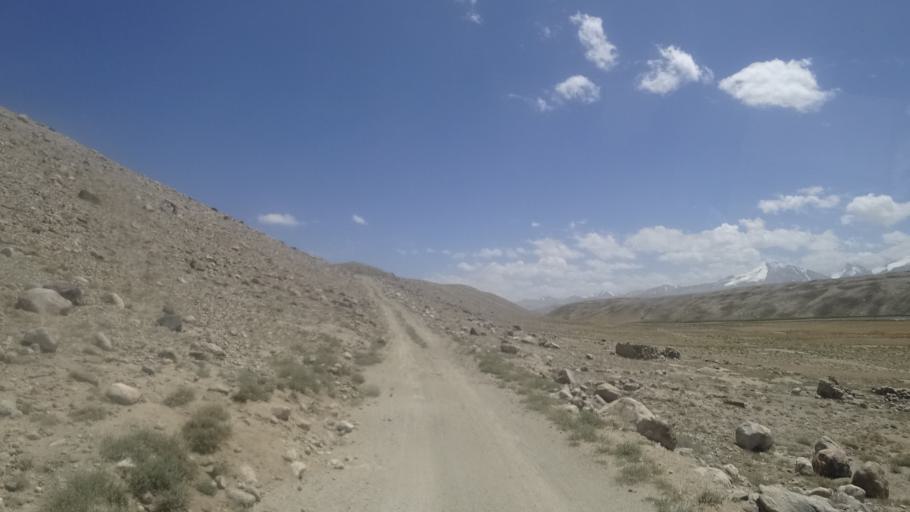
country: TJ
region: Gorno-Badakhshan
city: Murghob
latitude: 37.4643
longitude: 73.3500
